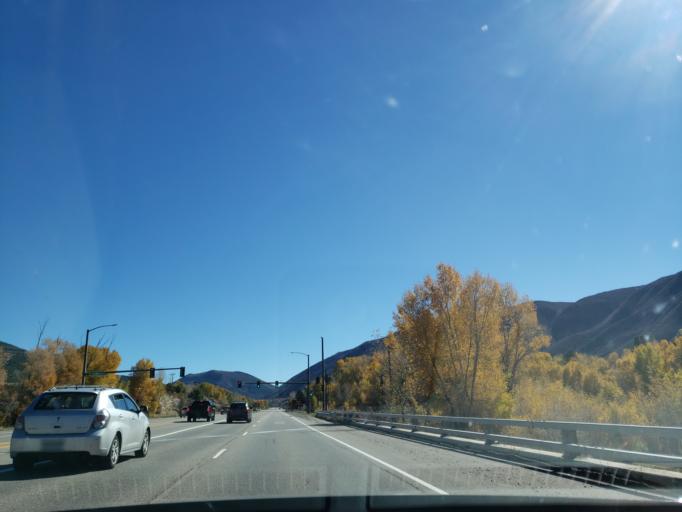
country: US
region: Colorado
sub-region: Eagle County
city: Basalt
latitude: 39.3594
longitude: -107.0275
